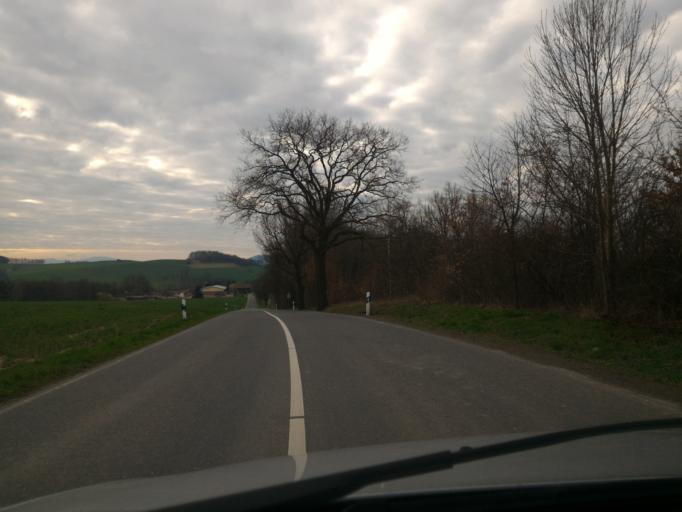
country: DE
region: Saxony
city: Hainewalde
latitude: 50.9212
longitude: 14.7015
